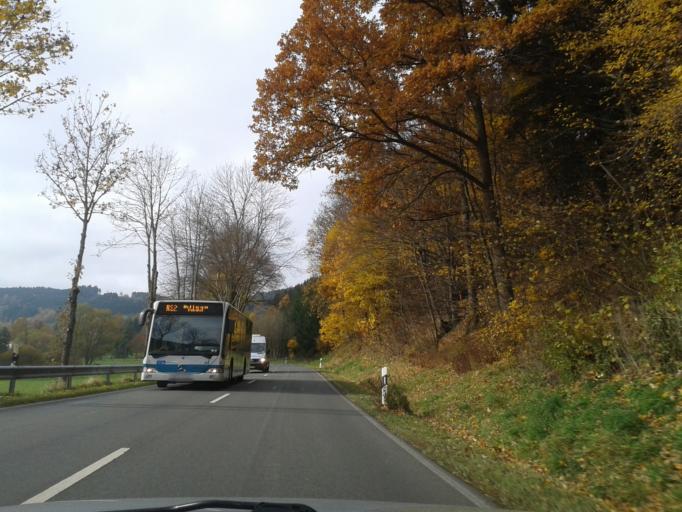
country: DE
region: North Rhine-Westphalia
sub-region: Regierungsbezirk Arnsberg
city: Bad Laasphe
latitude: 50.9234
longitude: 8.3706
